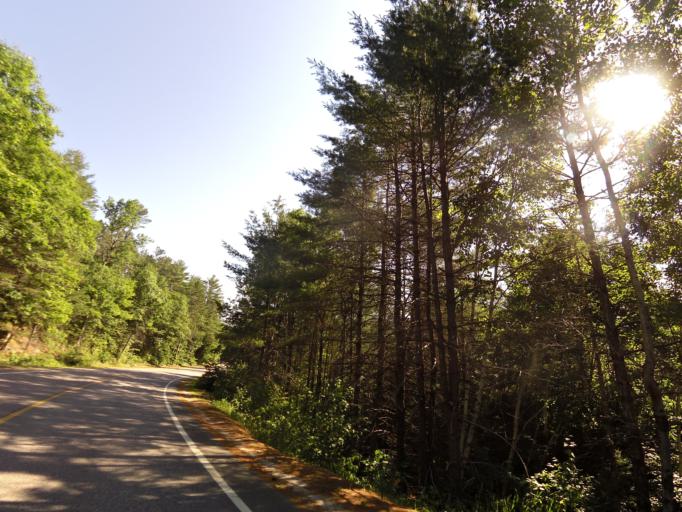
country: CA
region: Ontario
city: Deep River
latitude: 46.1954
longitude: -77.6844
